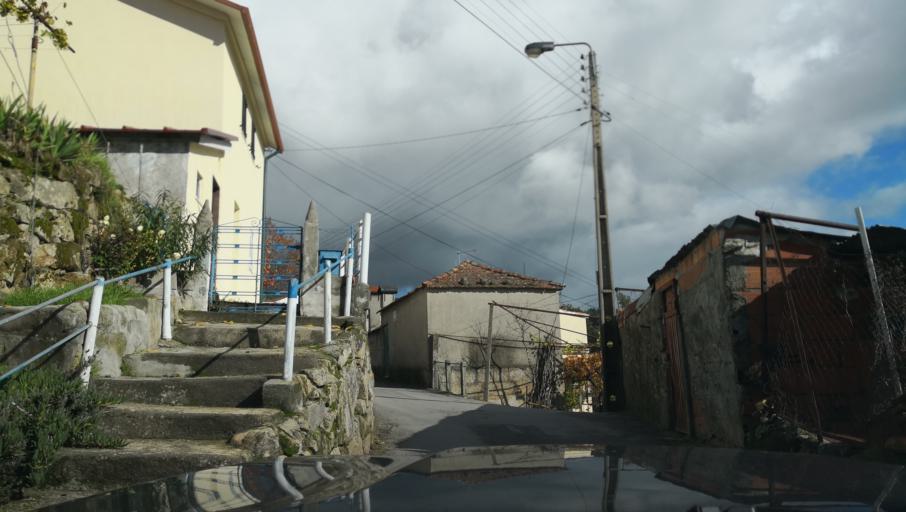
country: PT
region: Vila Real
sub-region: Vila Real
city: Vila Real
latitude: 41.3217
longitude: -7.7597
